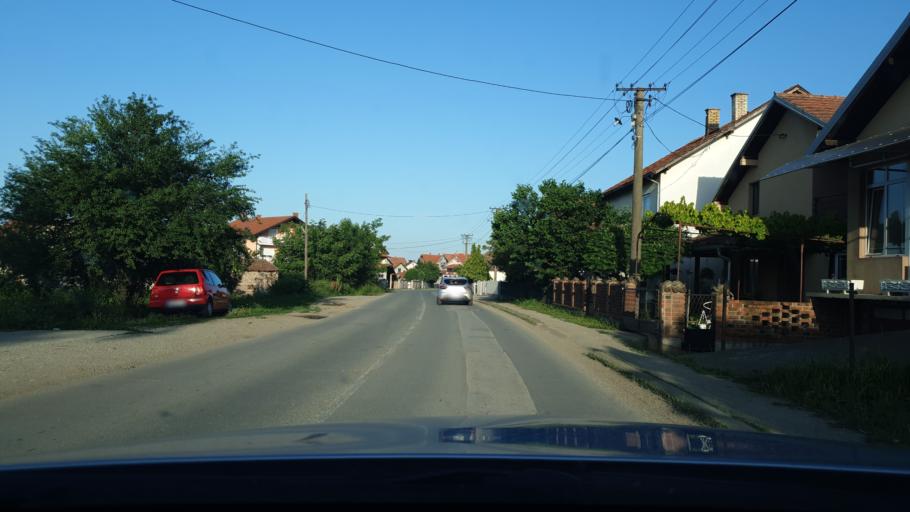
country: RS
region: Central Serbia
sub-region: Podunavski Okrug
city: Velika Plana
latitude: 44.3424
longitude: 21.0854
